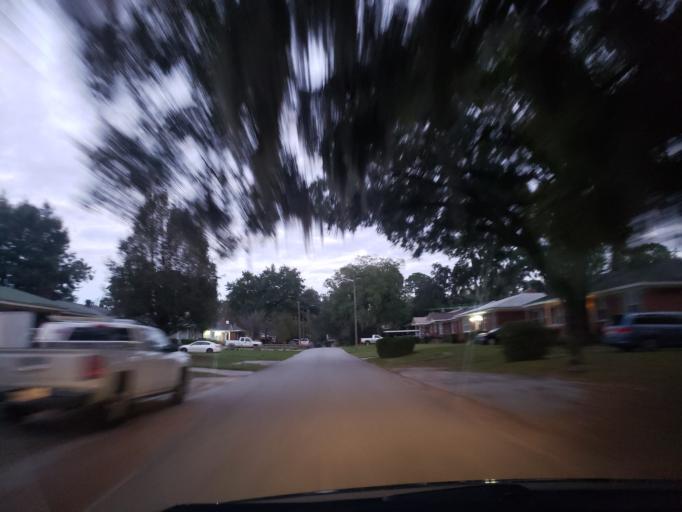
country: US
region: Georgia
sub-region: Chatham County
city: Thunderbolt
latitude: 32.0486
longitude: -81.0781
